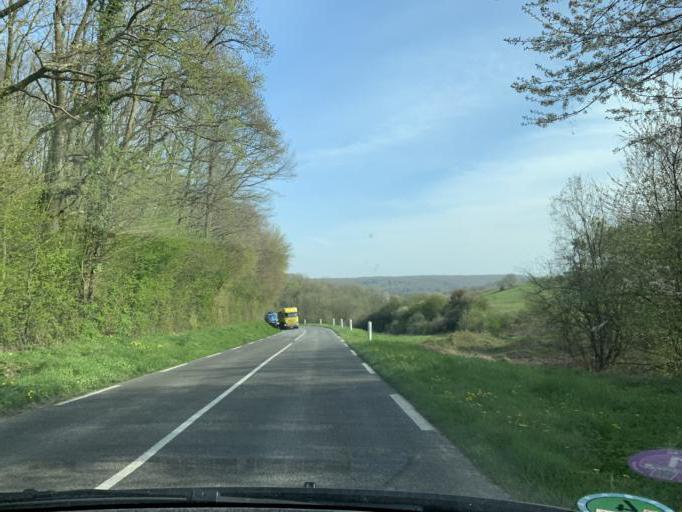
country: FR
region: Haute-Normandie
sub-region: Departement de l'Eure
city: Les Andelys
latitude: 49.2722
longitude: 1.4122
